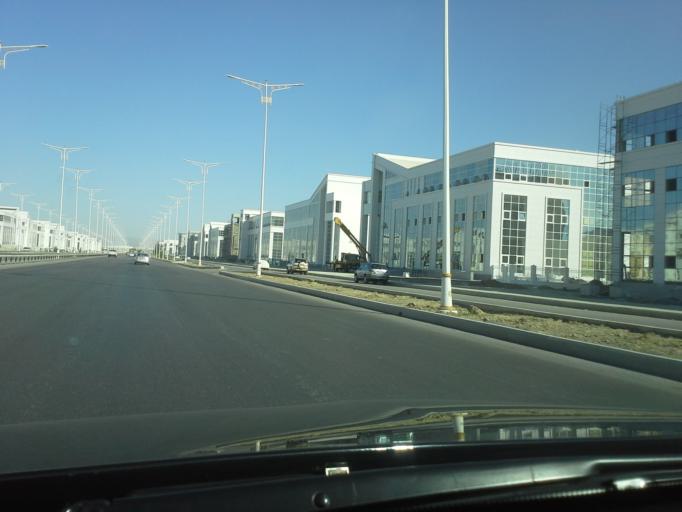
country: TM
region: Ahal
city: Ashgabat
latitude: 37.9702
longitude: 58.4043
